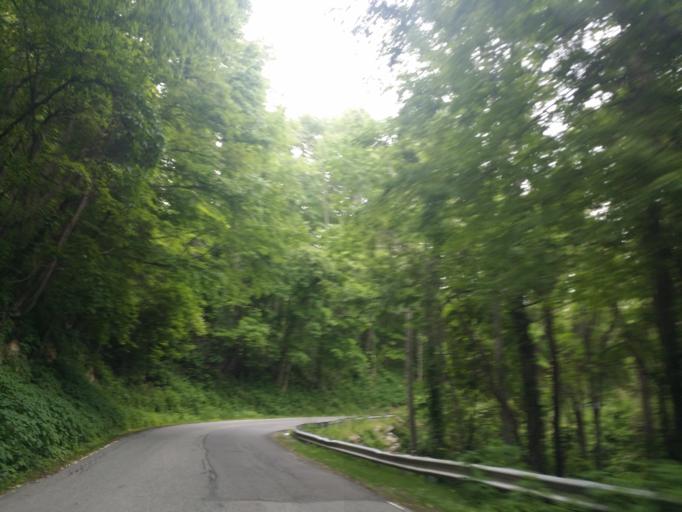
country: US
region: North Carolina
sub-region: Madison County
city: Marshall
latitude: 35.7071
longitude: -82.8278
